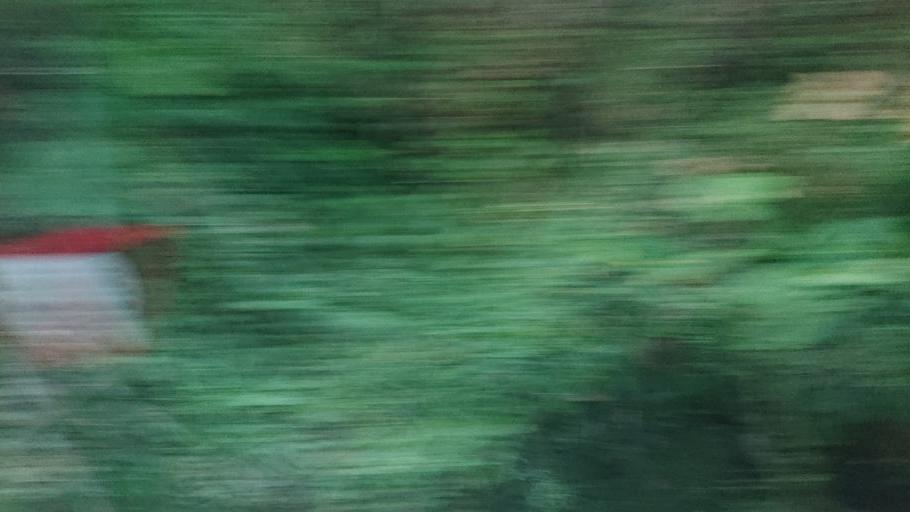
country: TW
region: Taiwan
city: Lugu
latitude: 23.5268
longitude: 120.7079
